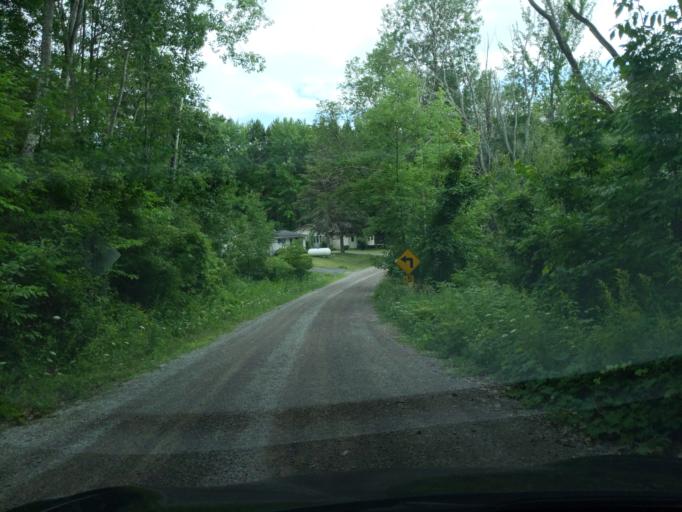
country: US
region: Michigan
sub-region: Clare County
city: Harrison
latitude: 43.9774
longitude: -85.0033
